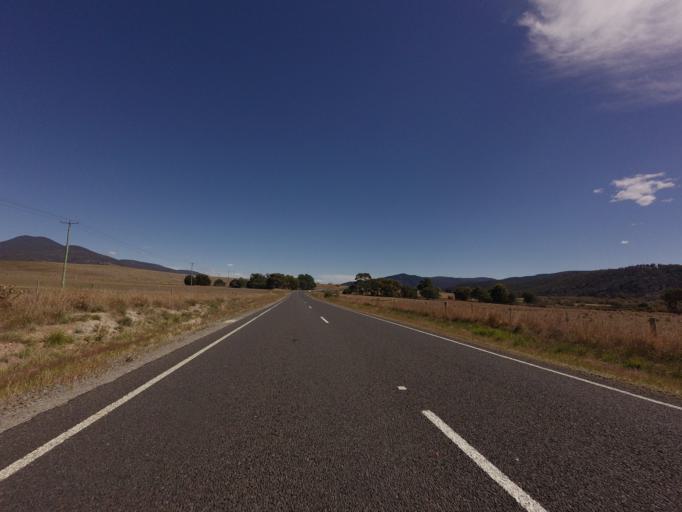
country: AU
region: Tasmania
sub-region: Break O'Day
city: St Helens
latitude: -41.7014
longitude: 147.8545
